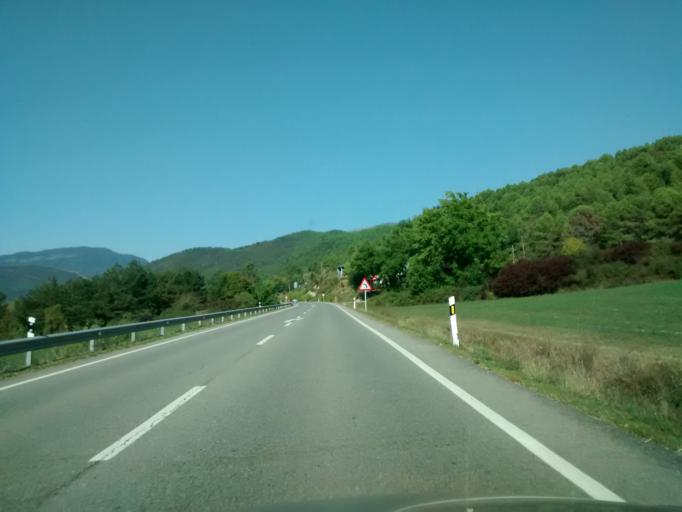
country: ES
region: Aragon
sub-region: Provincia de Huesca
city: Ainsa
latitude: 42.4301
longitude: 0.1137
